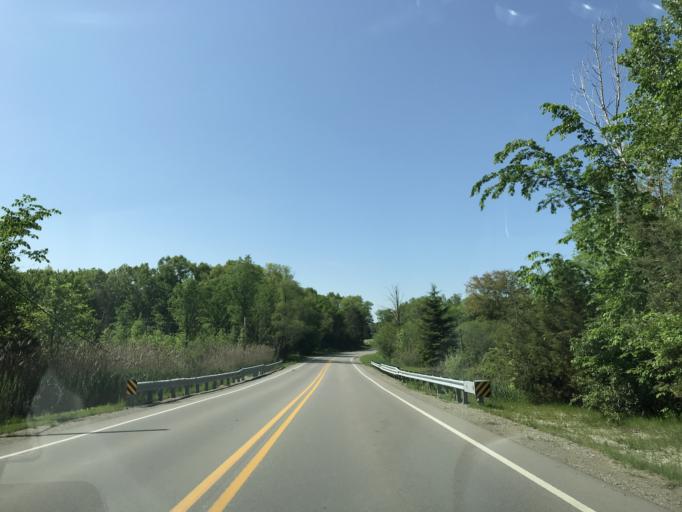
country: US
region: Michigan
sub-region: Oakland County
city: South Lyon
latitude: 42.4723
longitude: -83.6962
